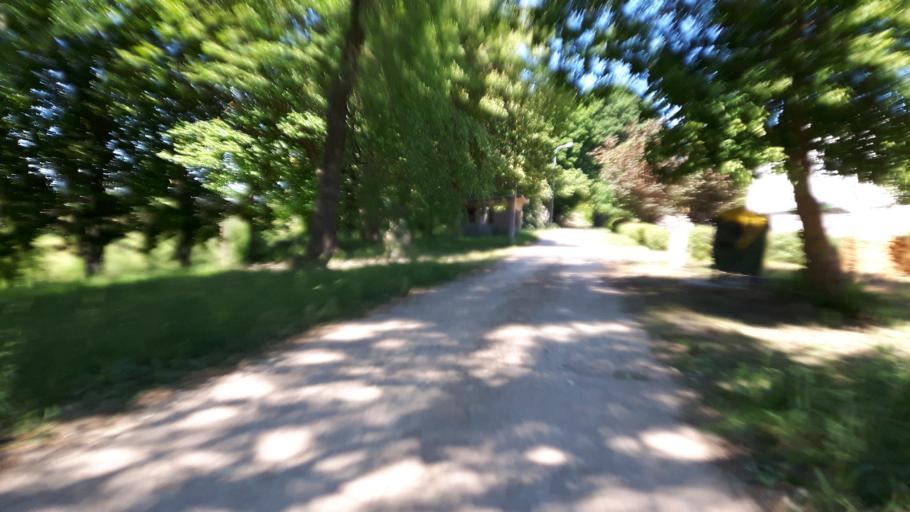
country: LV
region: Kandava
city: Kandava
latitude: 57.0365
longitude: 22.9034
